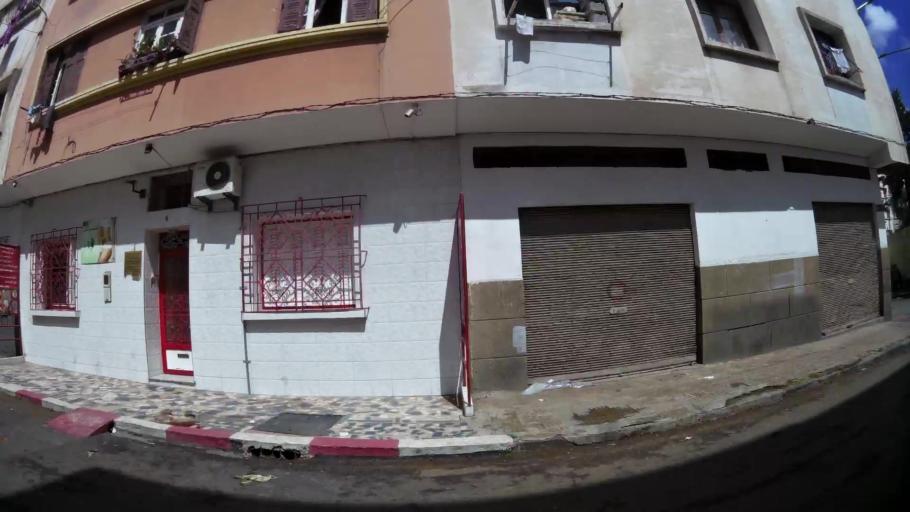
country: MA
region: Grand Casablanca
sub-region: Casablanca
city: Casablanca
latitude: 33.5594
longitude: -7.6070
